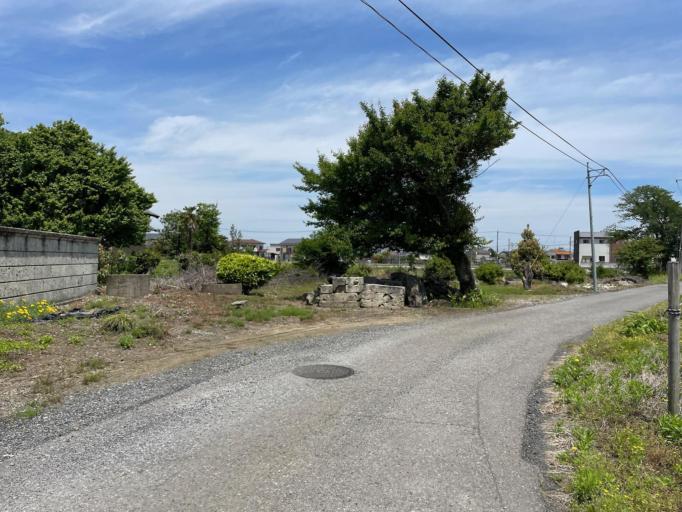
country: JP
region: Tochigi
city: Mibu
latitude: 36.4628
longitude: 139.7490
